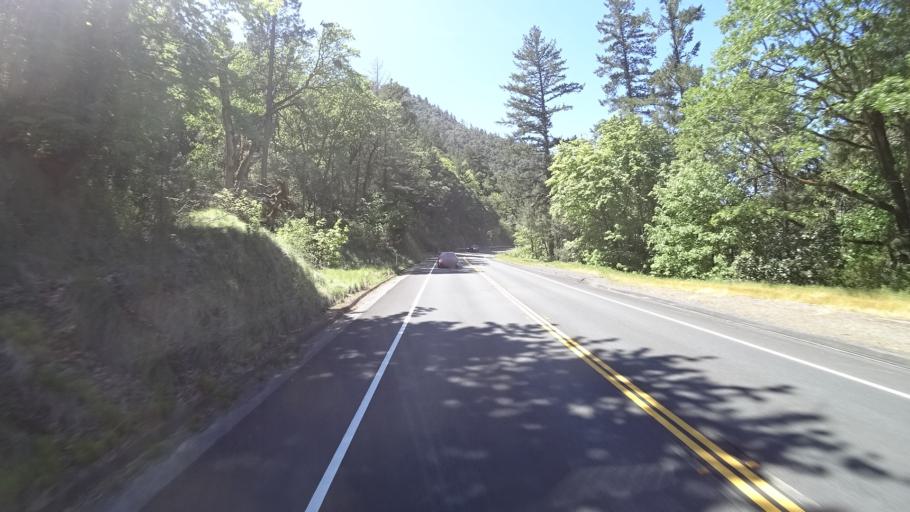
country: US
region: California
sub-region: Humboldt County
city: Willow Creek
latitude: 40.7895
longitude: -123.4496
